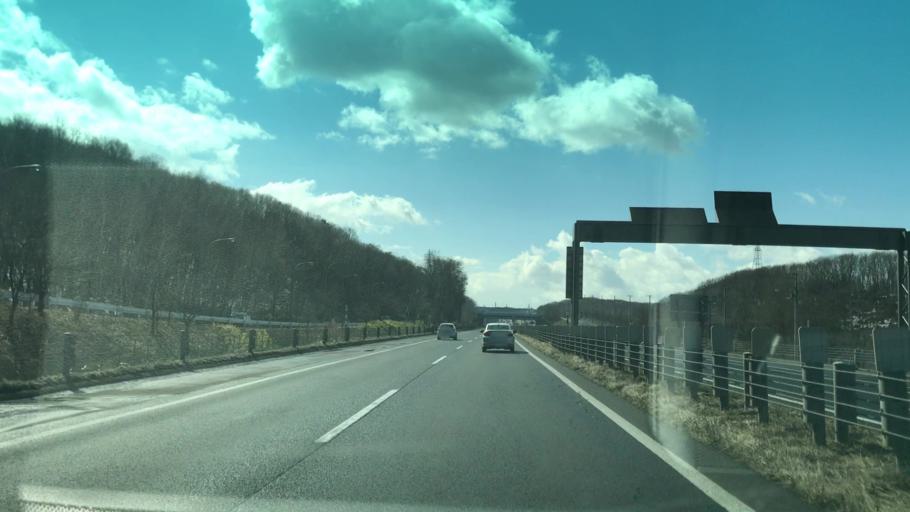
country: JP
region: Hokkaido
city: Kitahiroshima
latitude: 43.0064
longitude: 141.4669
